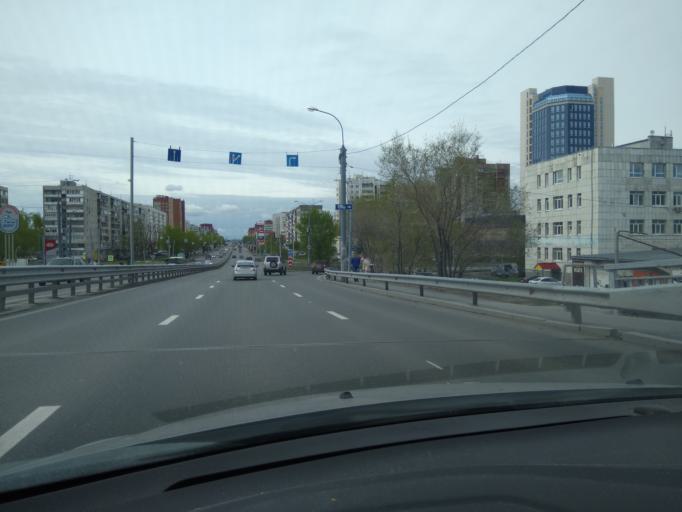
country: RU
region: Tjumen
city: Tyumen
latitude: 57.1218
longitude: 65.5831
